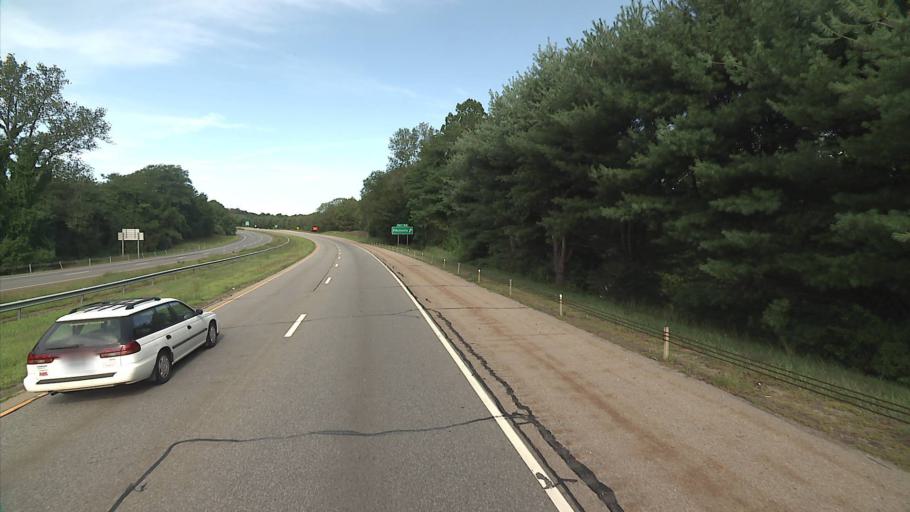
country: US
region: Connecticut
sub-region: New London County
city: Baltic
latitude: 41.5655
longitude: -72.1367
